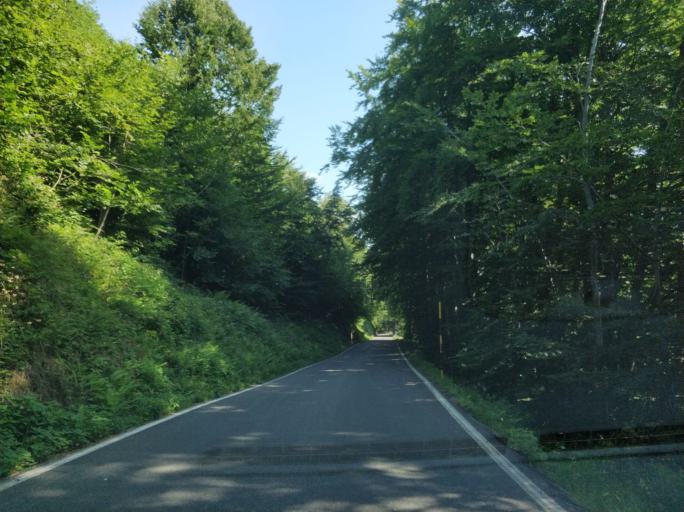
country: IT
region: Piedmont
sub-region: Provincia di Torino
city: Rubiana
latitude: 45.1830
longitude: 7.3709
